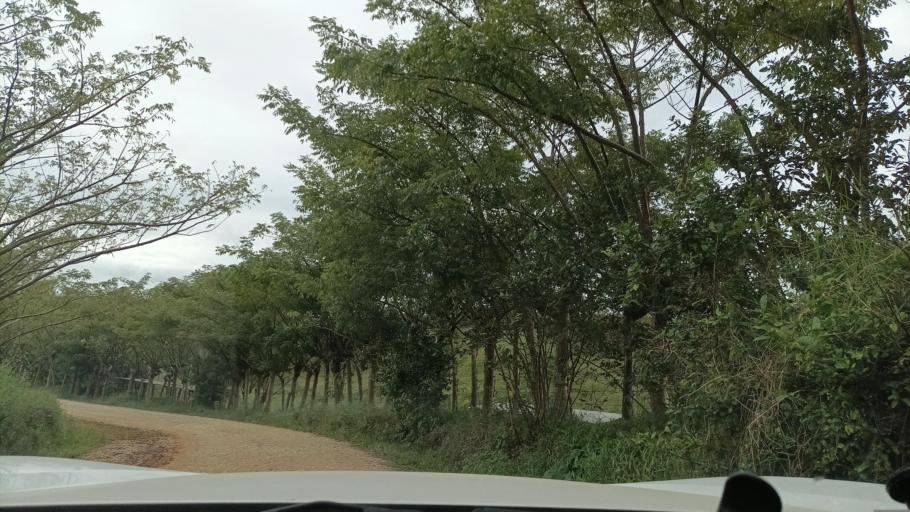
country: MX
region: Veracruz
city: Hidalgotitlan
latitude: 17.5965
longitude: -94.4213
